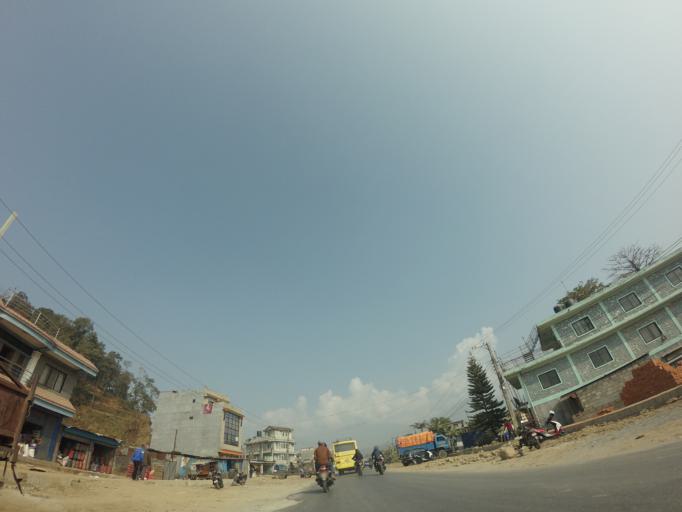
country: NP
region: Western Region
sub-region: Gandaki Zone
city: Pokhara
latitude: 28.2275
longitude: 83.9810
